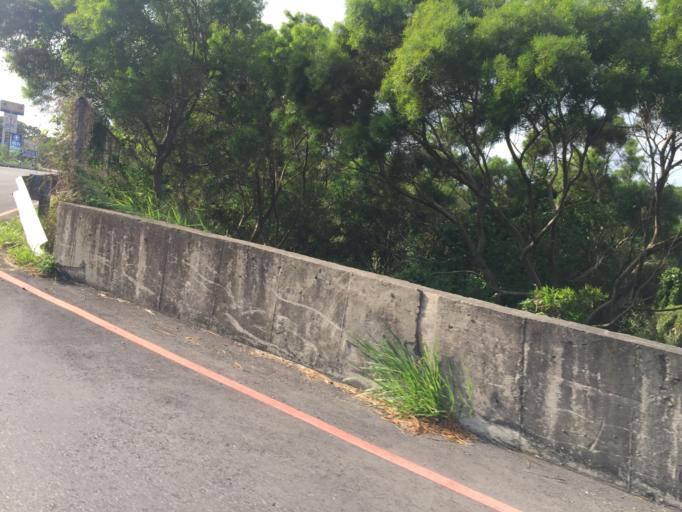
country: TW
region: Taiwan
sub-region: Hsinchu
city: Hsinchu
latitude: 24.7545
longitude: 120.9559
